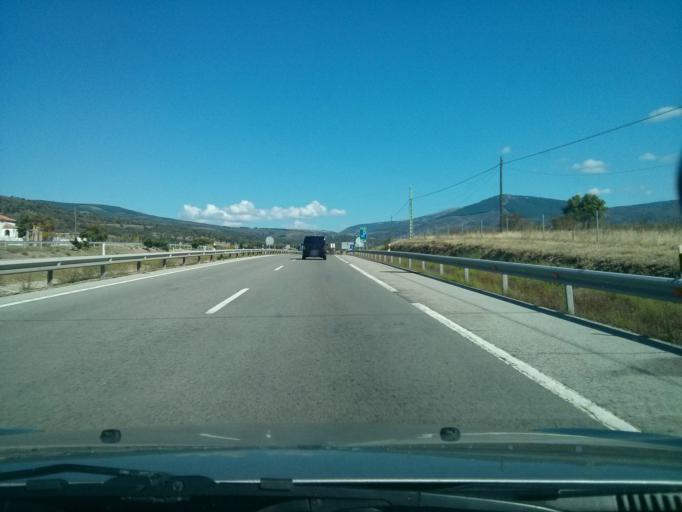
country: ES
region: Madrid
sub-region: Provincia de Madrid
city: Braojos
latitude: 41.0535
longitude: -3.6145
